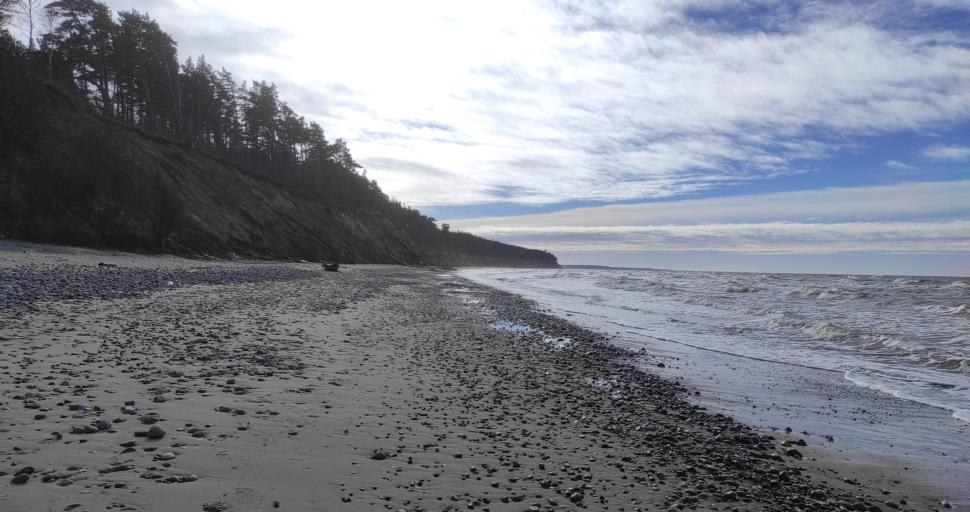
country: LV
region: Alsunga
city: Alsunga
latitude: 57.0307
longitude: 21.3980
